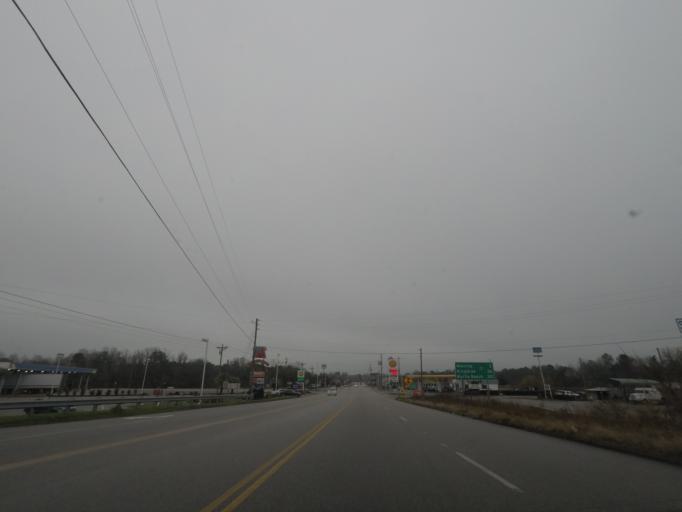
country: US
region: South Carolina
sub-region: Clarendon County
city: Manning
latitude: 33.7040
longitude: -80.2429
